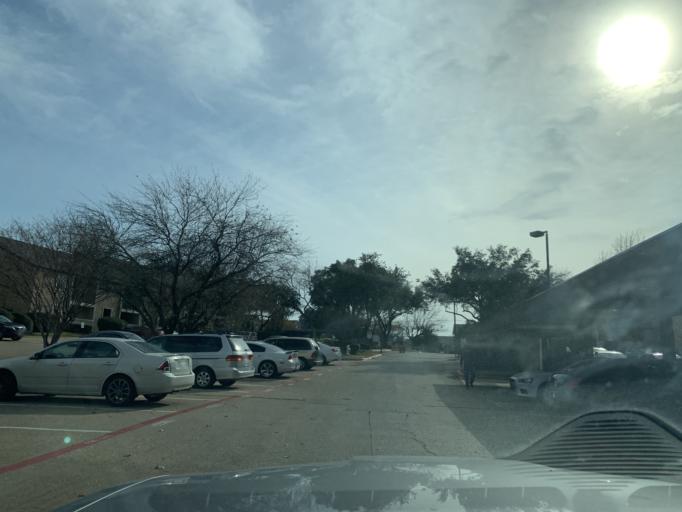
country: US
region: Texas
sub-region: Tarrant County
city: Euless
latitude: 32.7832
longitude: -97.0626
